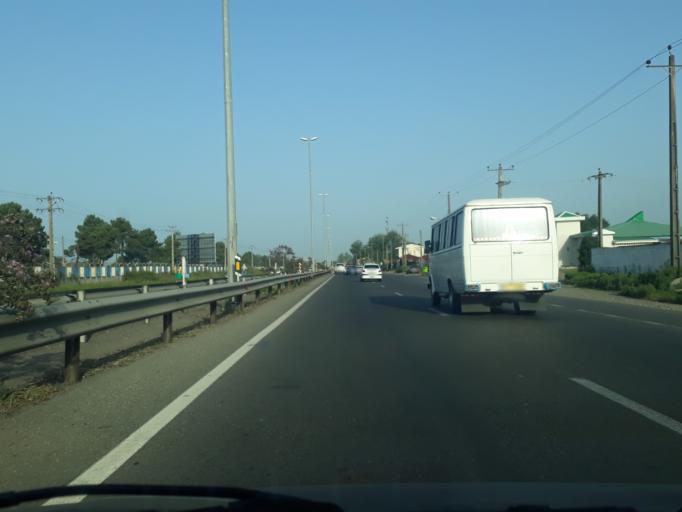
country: IR
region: Gilan
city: Bandar-e Anzali
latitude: 37.4587
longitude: 49.6004
